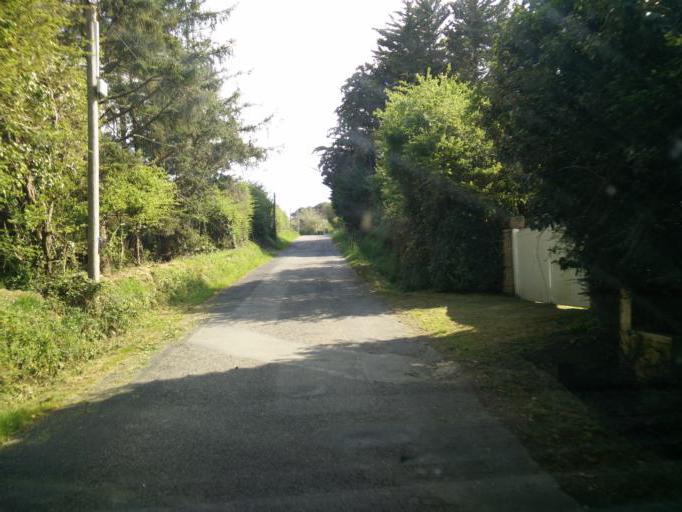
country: FR
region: Brittany
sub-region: Departement du Finistere
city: Crozon
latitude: 48.2356
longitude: -4.5440
